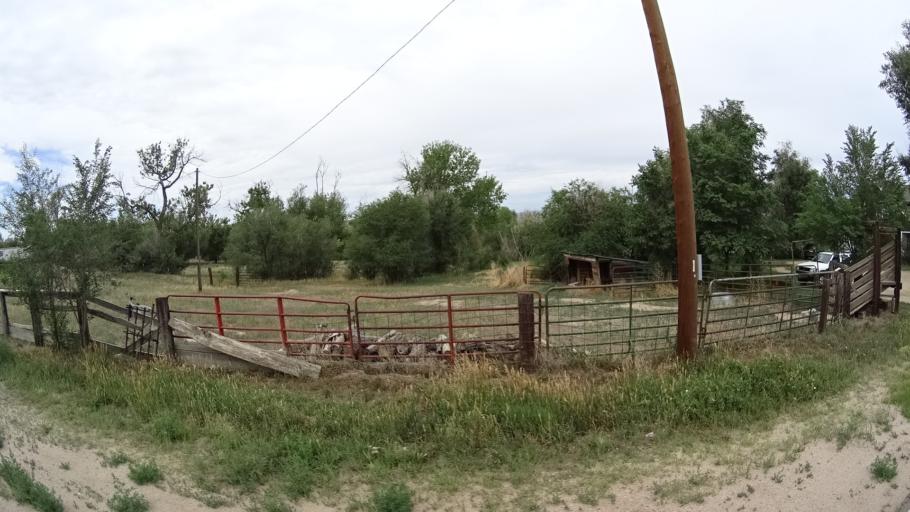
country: US
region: Colorado
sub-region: El Paso County
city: Fountain
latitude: 38.6688
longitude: -104.6944
